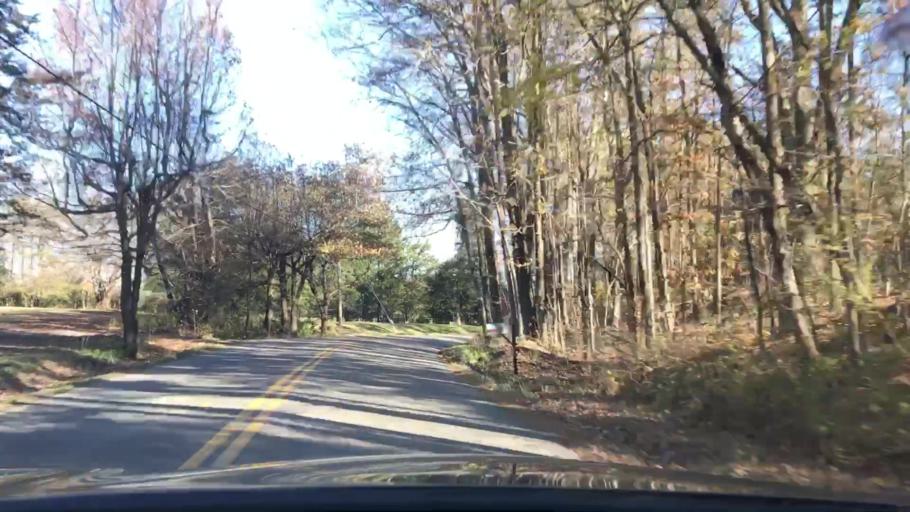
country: US
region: Virginia
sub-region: Henrico County
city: Short Pump
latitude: 37.6673
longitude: -77.7047
